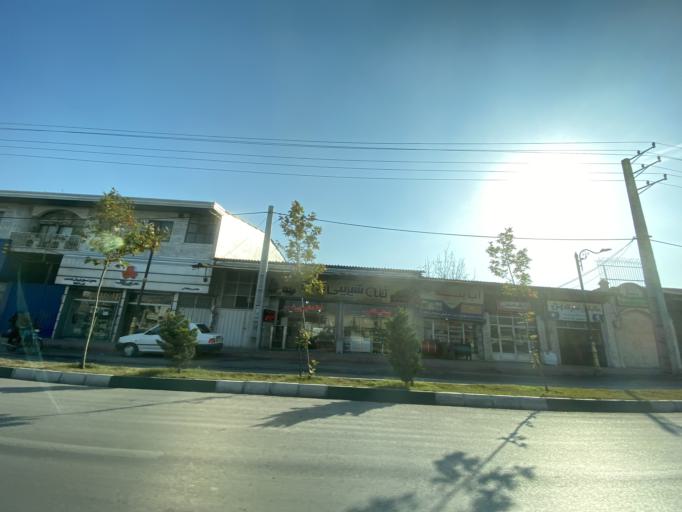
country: IR
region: Mazandaran
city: Babol
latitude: 36.5356
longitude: 52.6588
